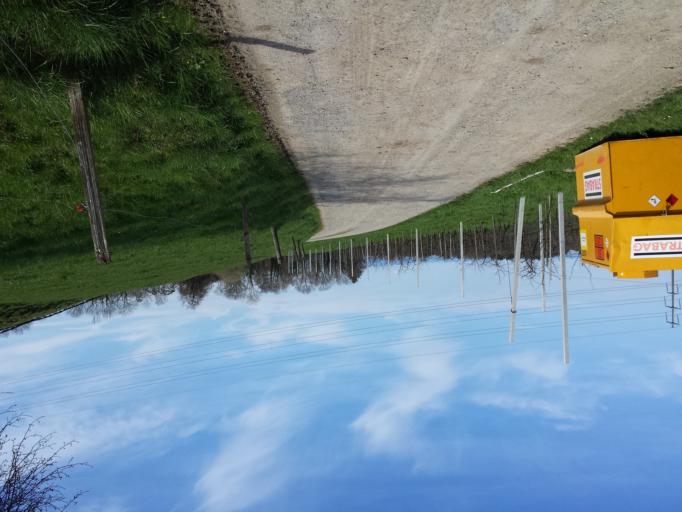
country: CH
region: Thurgau
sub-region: Arbon District
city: Amriswil
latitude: 47.5392
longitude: 9.3124
